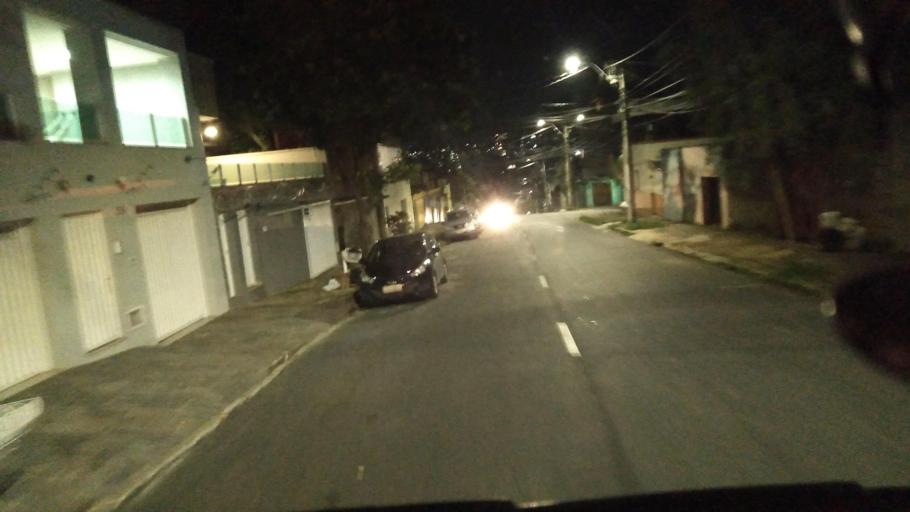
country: BR
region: Minas Gerais
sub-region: Belo Horizonte
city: Belo Horizonte
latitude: -19.9128
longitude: -43.9148
